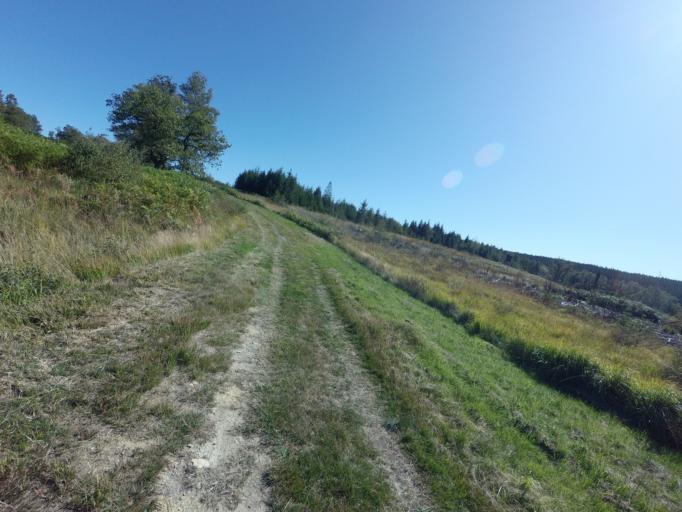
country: DE
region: North Rhine-Westphalia
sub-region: Regierungsbezirk Koln
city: Roetgen
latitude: 50.5923
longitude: 6.1483
